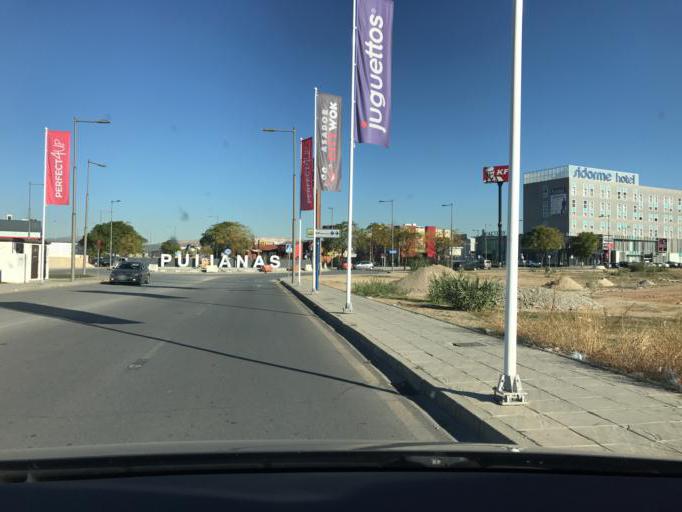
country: ES
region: Andalusia
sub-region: Provincia de Granada
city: Maracena
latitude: 37.2107
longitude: -3.6200
